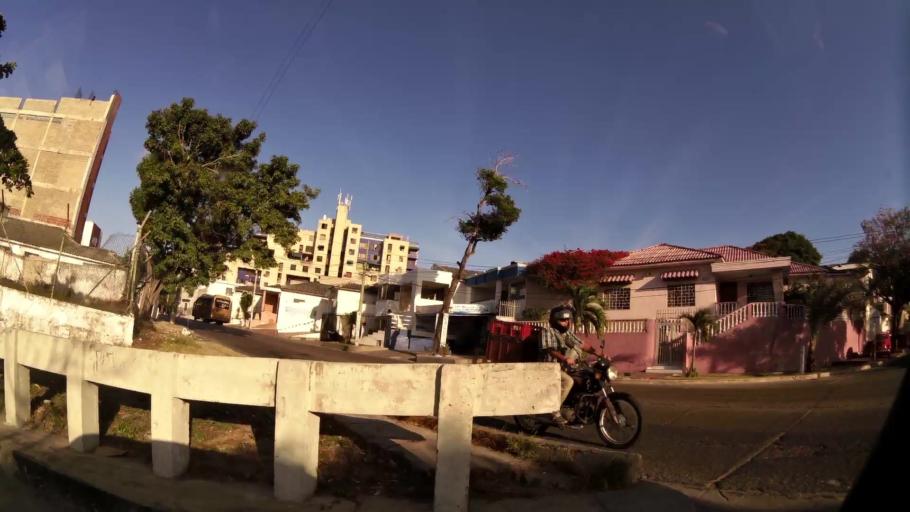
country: CO
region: Atlantico
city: Barranquilla
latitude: 10.9835
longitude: -74.8014
